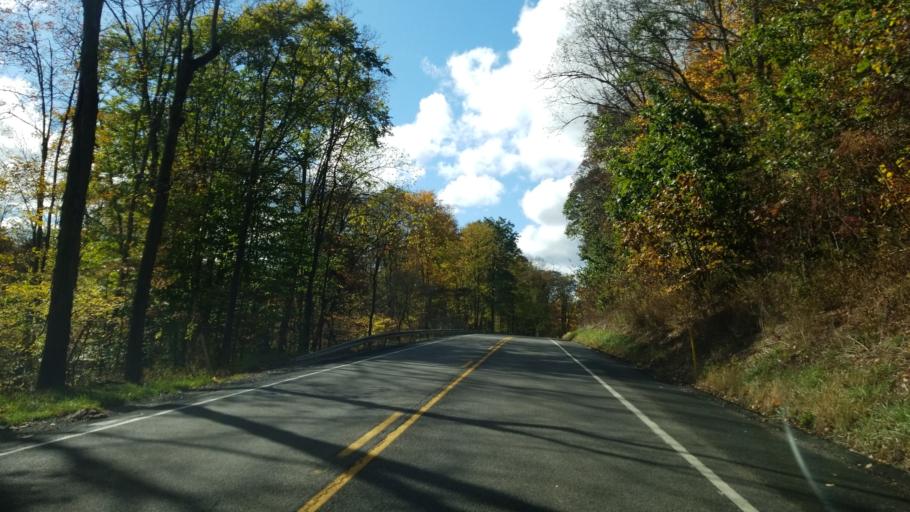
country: US
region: Pennsylvania
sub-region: Jefferson County
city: Sykesville
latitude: 41.0915
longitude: -78.8306
